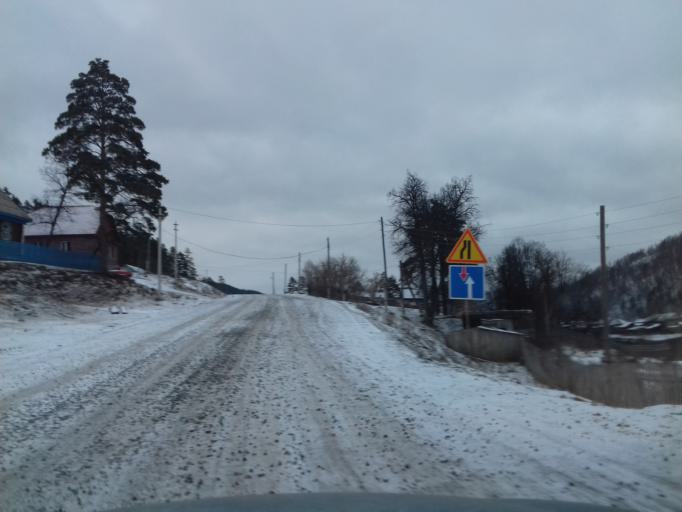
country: RU
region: Bashkortostan
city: Starosubkhangulovo
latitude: 53.0924
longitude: 57.4266
